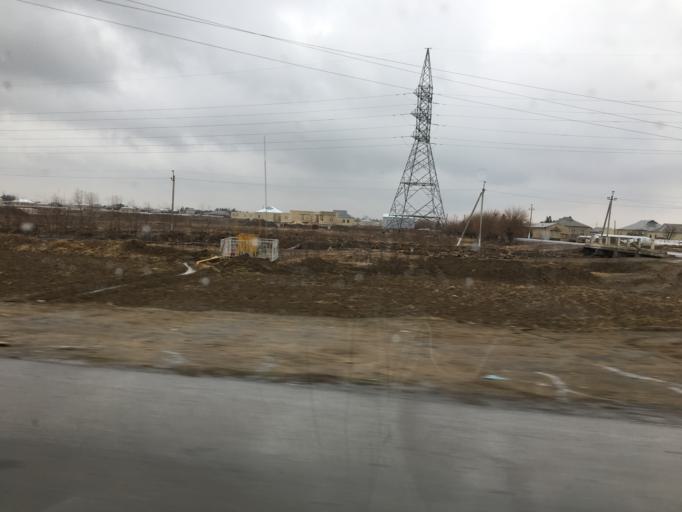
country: TM
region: Mary
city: Mary
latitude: 37.5373
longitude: 61.8825
